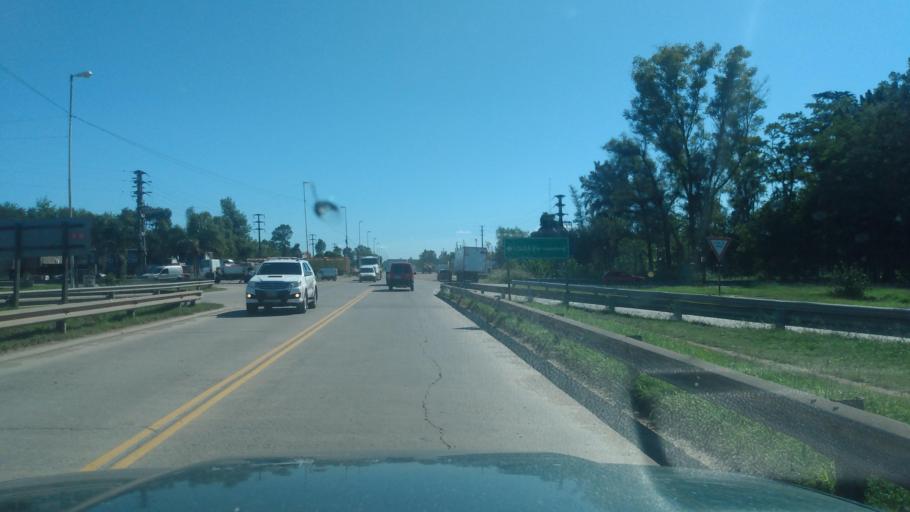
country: AR
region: Buenos Aires
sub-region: Partido de General Rodriguez
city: General Rodriguez
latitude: -34.5924
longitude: -58.9474
